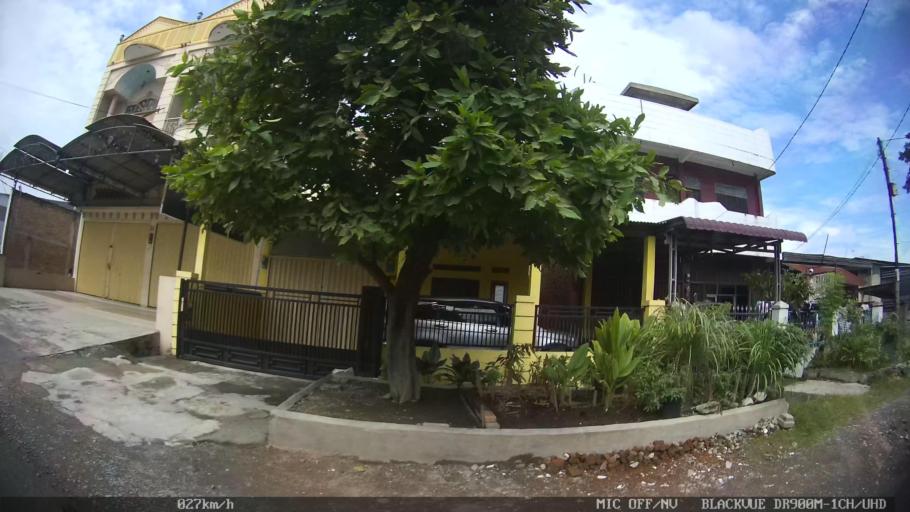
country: ID
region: North Sumatra
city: Medan
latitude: 3.5872
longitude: 98.7343
